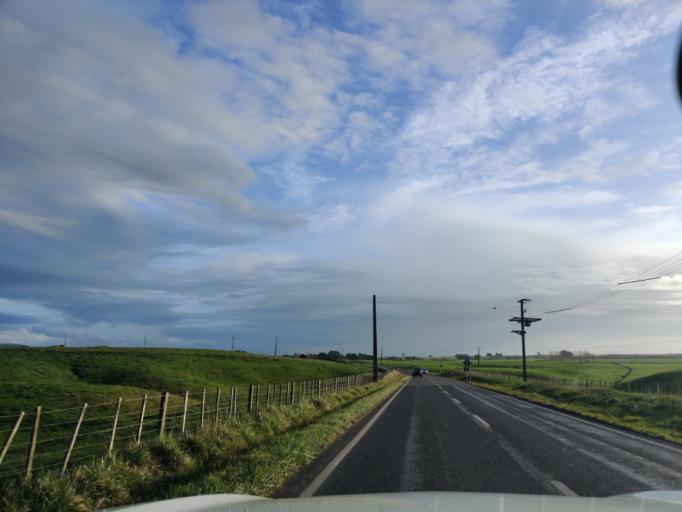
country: NZ
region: Manawatu-Wanganui
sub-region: Palmerston North City
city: Palmerston North
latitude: -40.4978
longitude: 175.4921
